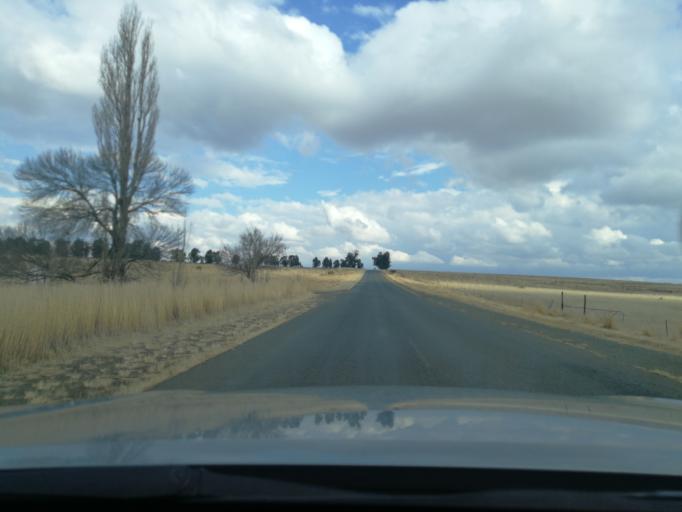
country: ZA
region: Orange Free State
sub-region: Fezile Dabi District Municipality
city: Frankfort
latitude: -27.4105
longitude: 28.5063
